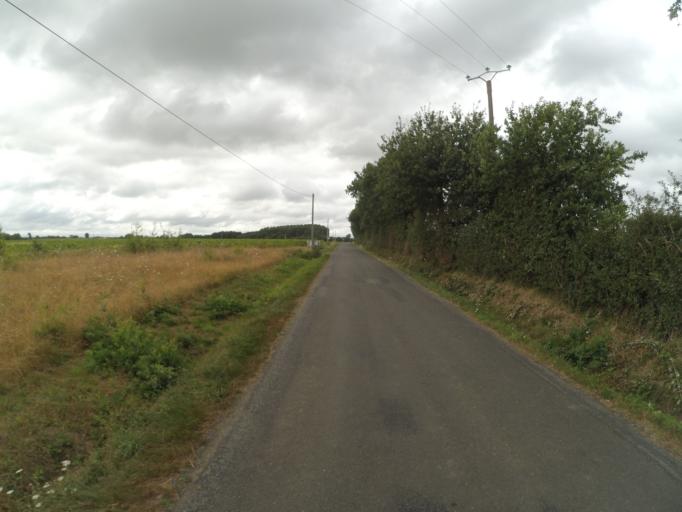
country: FR
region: Pays de la Loire
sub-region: Departement de la Vendee
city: Saint-Philbert-de-Bouaine
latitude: 46.9965
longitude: -1.5251
